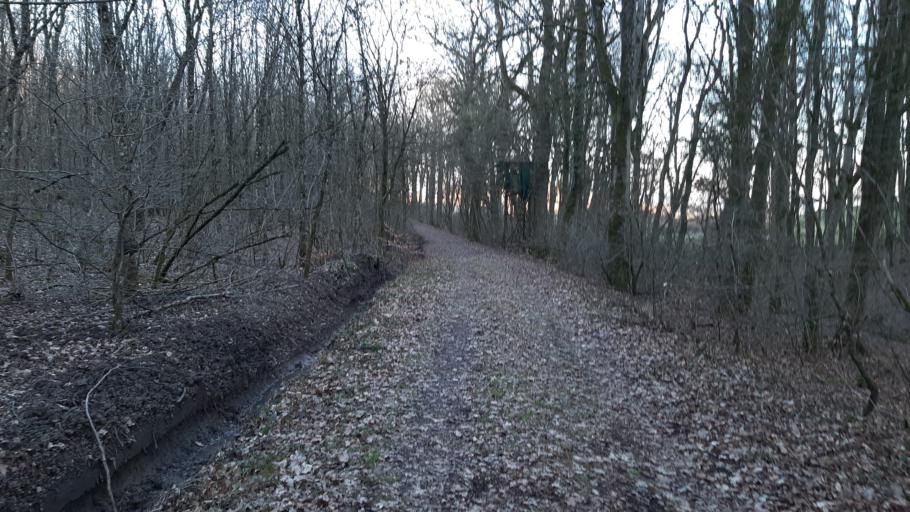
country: LU
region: Grevenmacher
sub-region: Canton d'Echternach
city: Mompach
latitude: 49.7388
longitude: 6.4860
